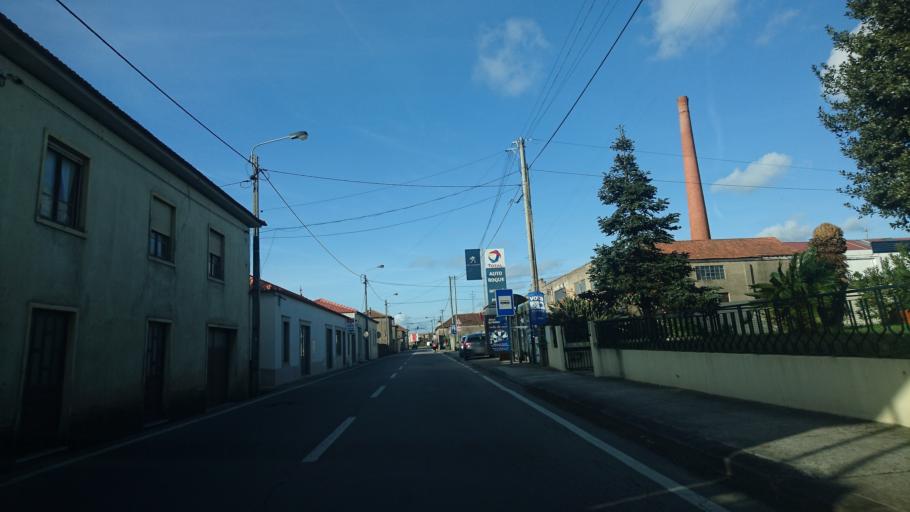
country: PT
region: Aveiro
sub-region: Ovar
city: Esmoriz
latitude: 40.9678
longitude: -8.6291
